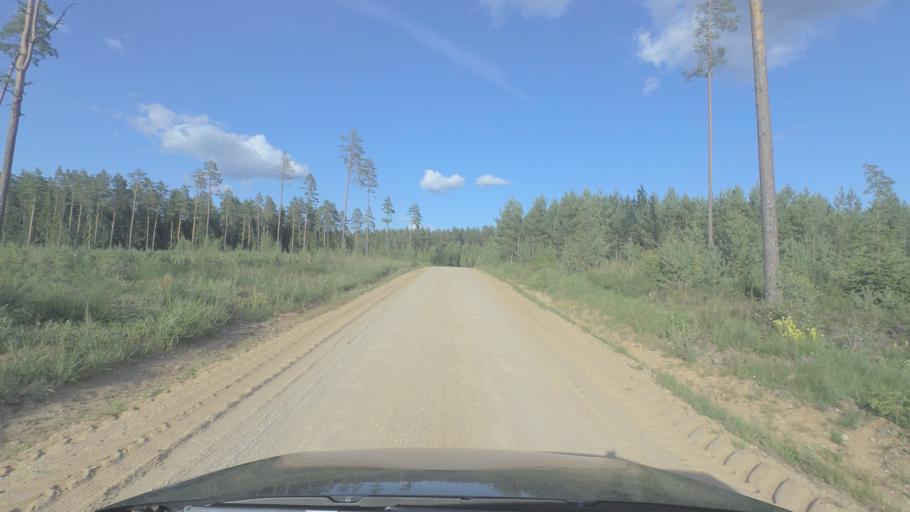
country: LT
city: Pabrade
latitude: 55.1544
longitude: 25.7873
